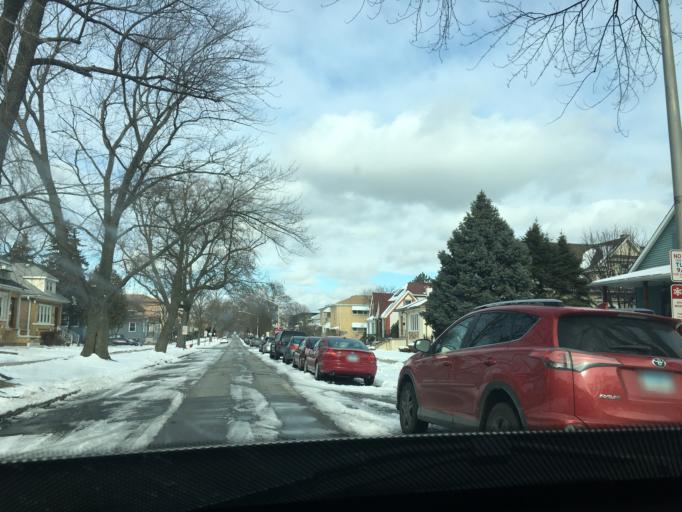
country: US
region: Illinois
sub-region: Cook County
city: Elmwood Park
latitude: 41.9282
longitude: -87.8125
